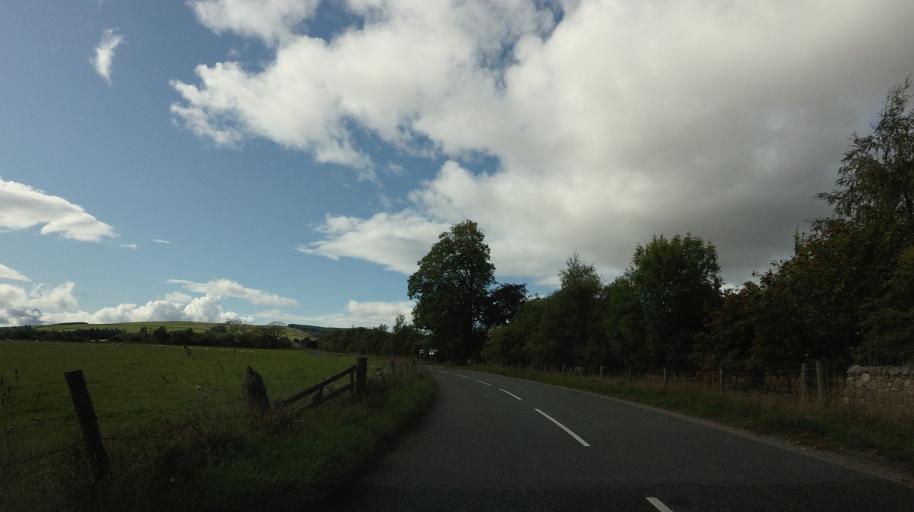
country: GB
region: Scotland
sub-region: Aberdeenshire
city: Alford
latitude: 57.2324
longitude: -2.7440
